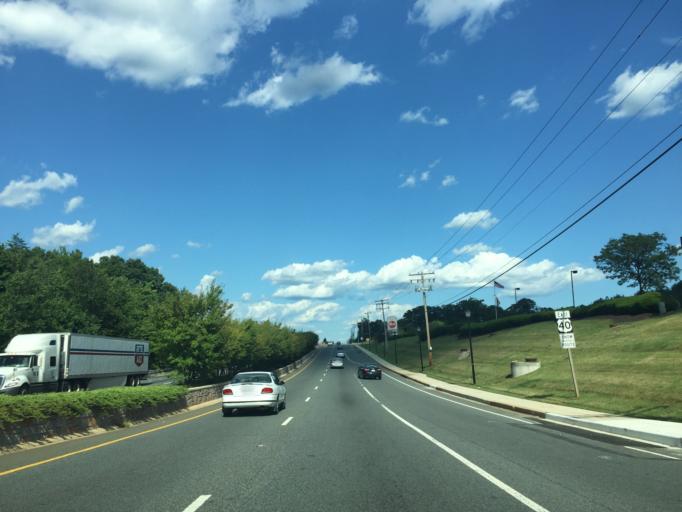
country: US
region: Maryland
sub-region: Harford County
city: Edgewood
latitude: 39.4333
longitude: -76.3274
